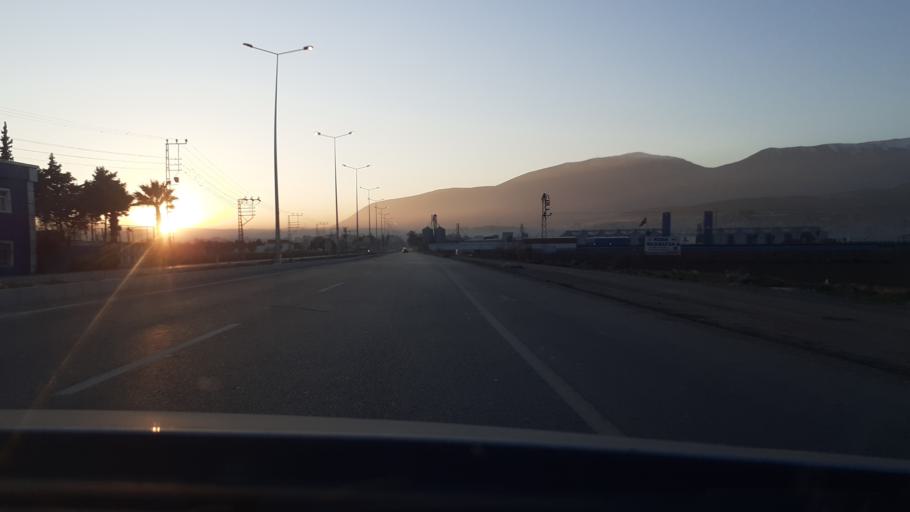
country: TR
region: Hatay
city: Kirikhan
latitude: 36.5018
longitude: 36.3876
